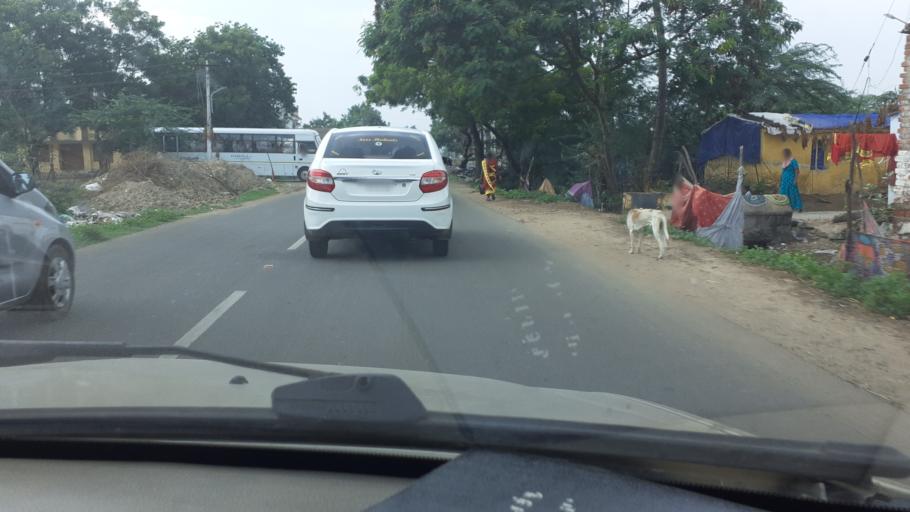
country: IN
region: Tamil Nadu
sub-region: Tirunelveli Kattabo
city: Viravanallur
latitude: 8.7185
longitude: 77.5491
